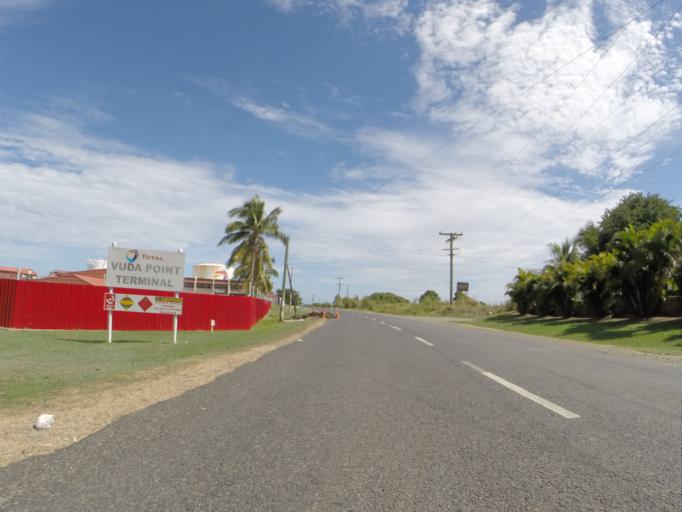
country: FJ
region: Western
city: Lautoka
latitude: -17.6809
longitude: 177.3924
